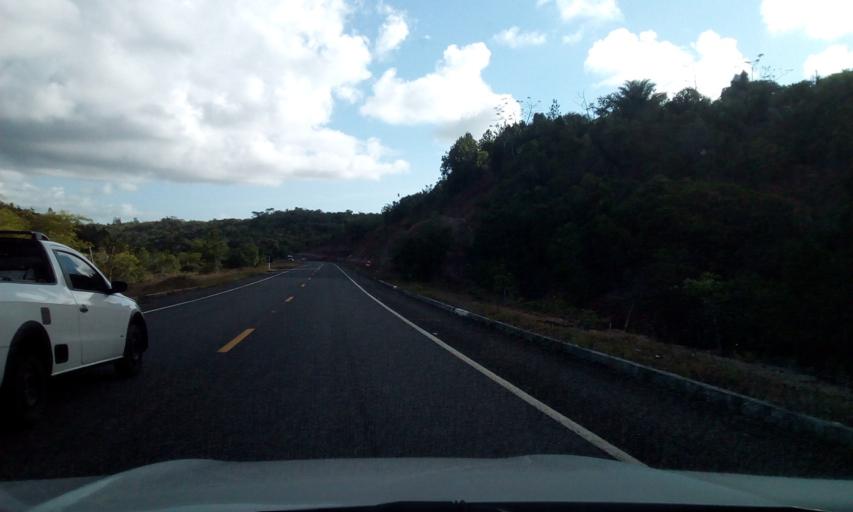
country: BR
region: Bahia
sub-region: Conde
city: Conde
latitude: -12.0756
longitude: -37.7539
